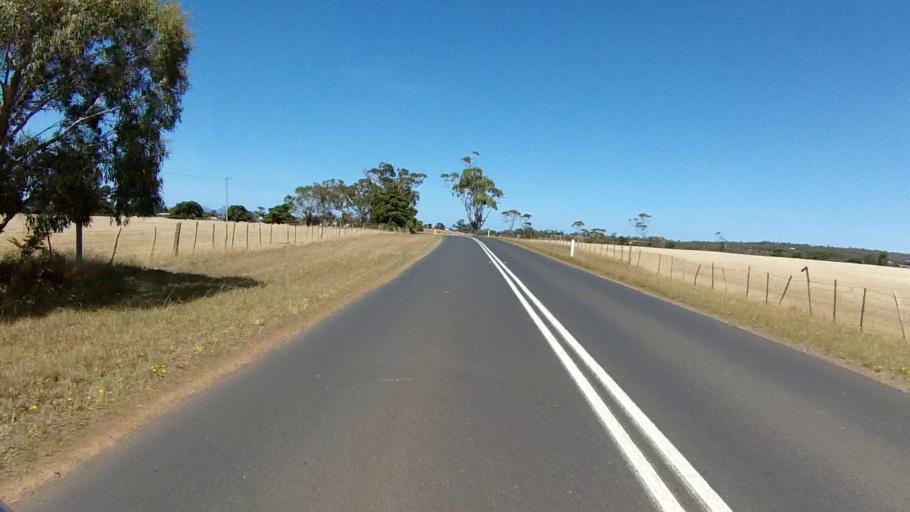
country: AU
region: Tasmania
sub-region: Break O'Day
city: St Helens
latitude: -42.1174
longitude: 148.0623
